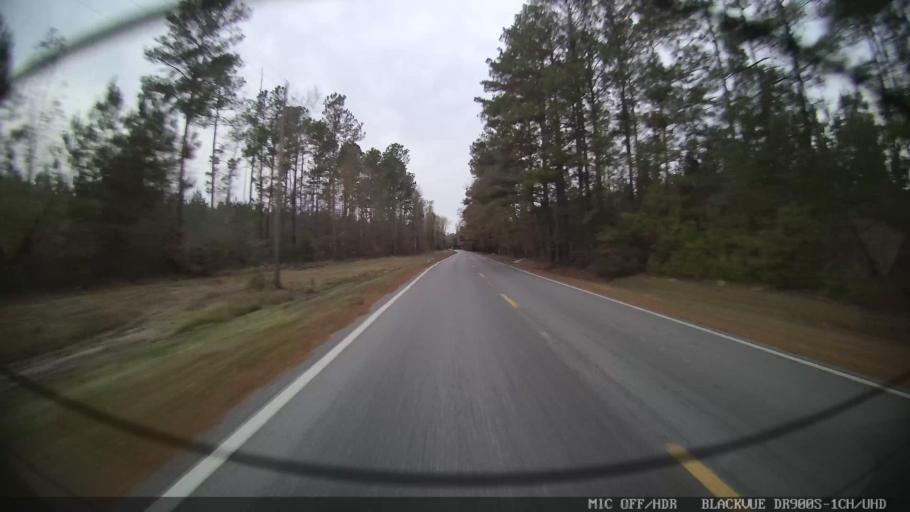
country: US
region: Mississippi
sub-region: Clarke County
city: Quitman
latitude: 32.0241
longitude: -88.8451
